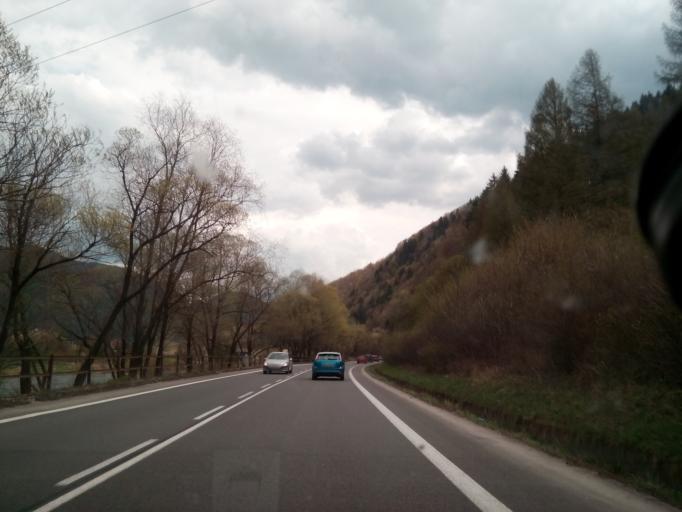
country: SK
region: Zilinsky
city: Ruzomberok
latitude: 49.1207
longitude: 19.2056
